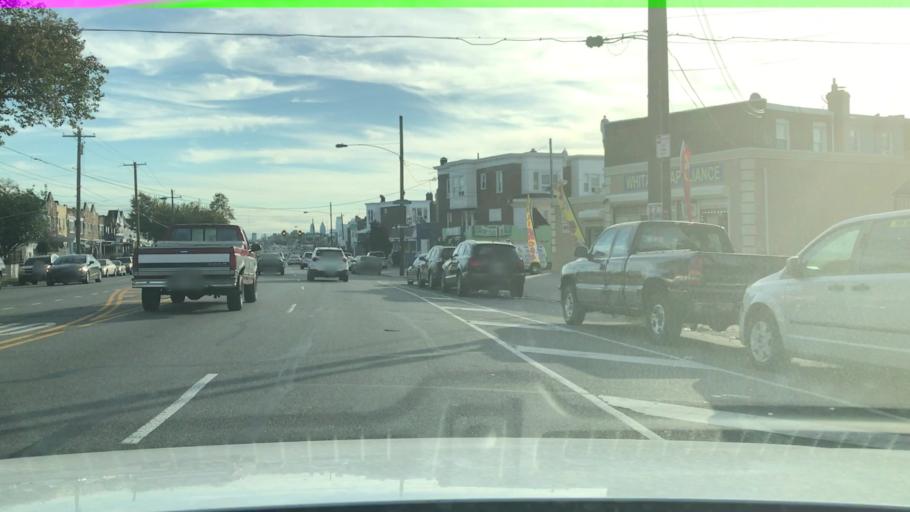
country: US
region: Pennsylvania
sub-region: Montgomery County
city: Rockledge
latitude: 40.0201
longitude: -75.1144
